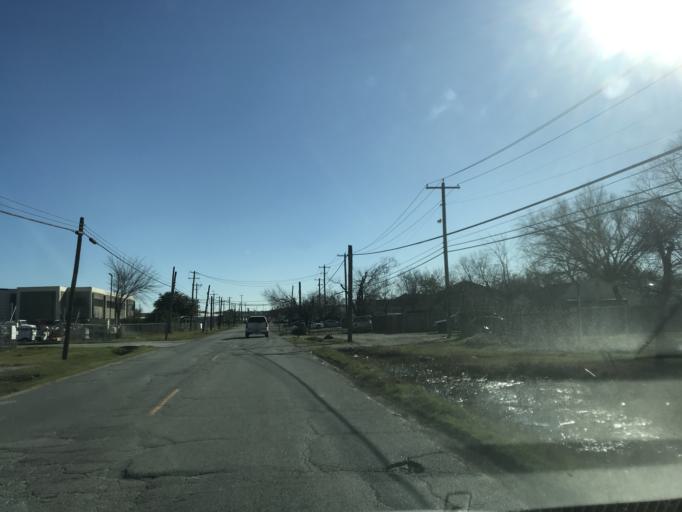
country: US
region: Texas
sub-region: Dallas County
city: Cockrell Hill
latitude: 32.7747
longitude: -96.9045
